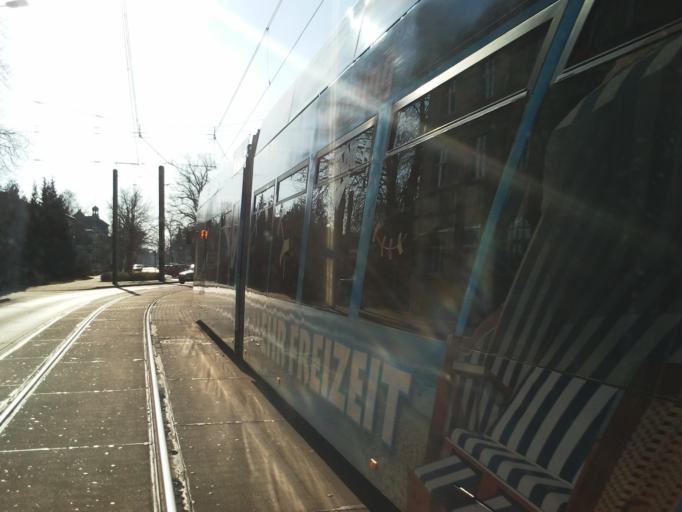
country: DE
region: Mecklenburg-Vorpommern
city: Rostock
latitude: 54.0821
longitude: 12.1408
